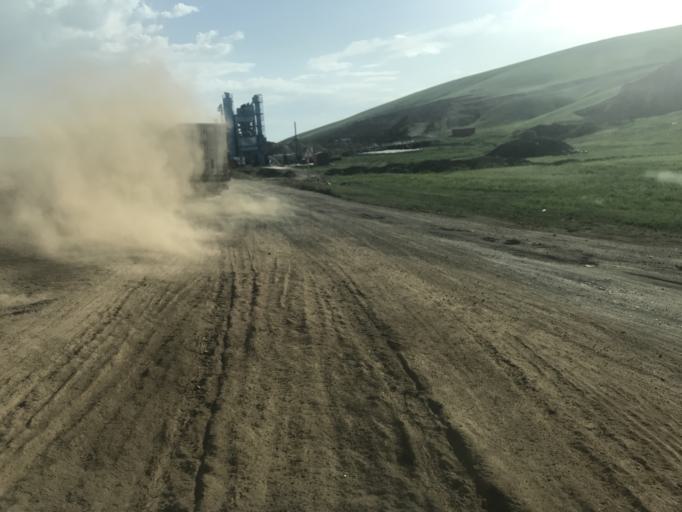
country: MN
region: Central Aimak
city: Bornuur
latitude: 48.6821
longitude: 106.1485
